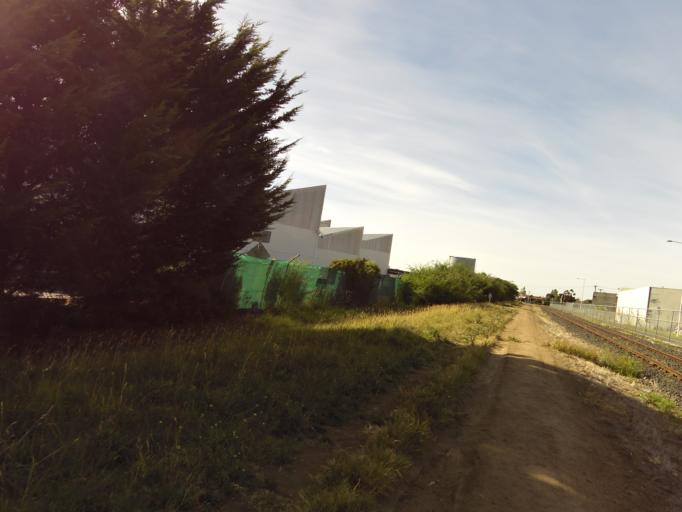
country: AU
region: Tasmania
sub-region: Glenorchy
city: Moonah
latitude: -42.8438
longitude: 147.2959
